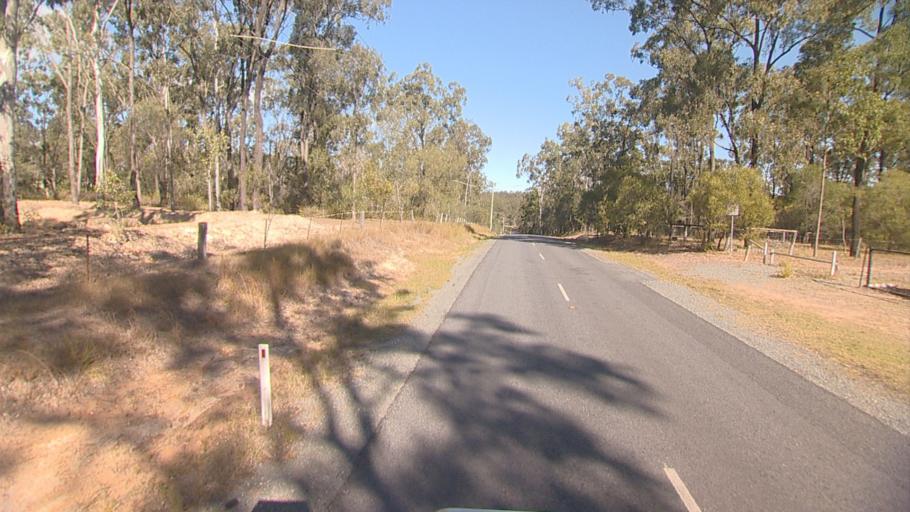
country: AU
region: Queensland
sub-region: Logan
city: Chambers Flat
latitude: -27.8112
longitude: 153.0718
